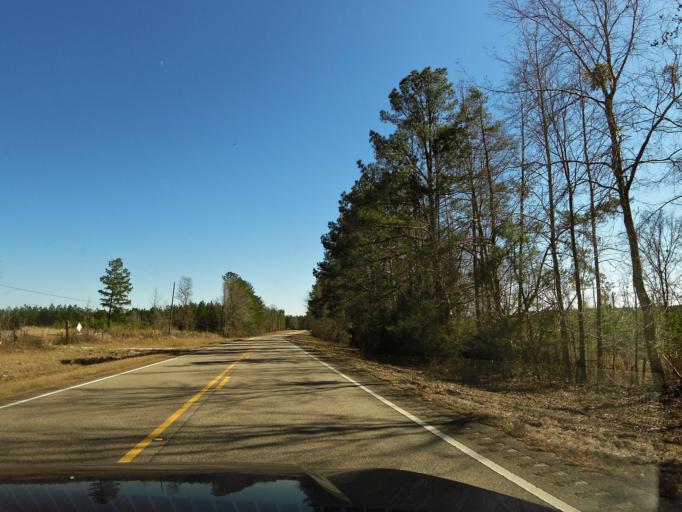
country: US
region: Alabama
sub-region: Montgomery County
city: Pike Road
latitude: 32.1679
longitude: -86.0654
